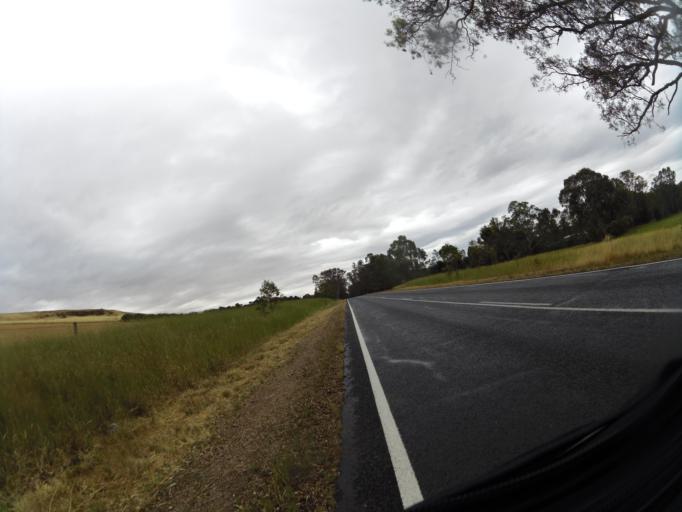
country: AU
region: Victoria
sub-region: Mount Alexander
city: Castlemaine
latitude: -37.1522
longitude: 144.0416
